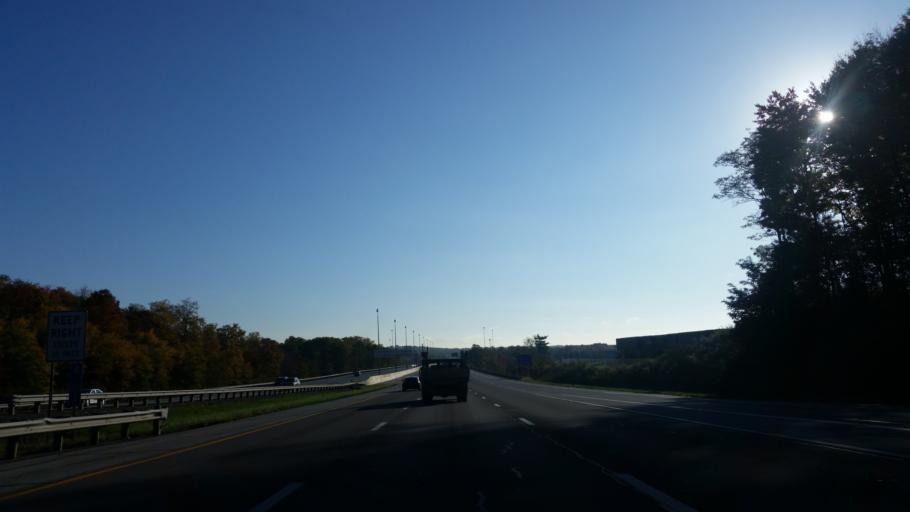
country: US
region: Ohio
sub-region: Summit County
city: Montrose-Ghent
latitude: 41.1193
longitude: -81.6463
